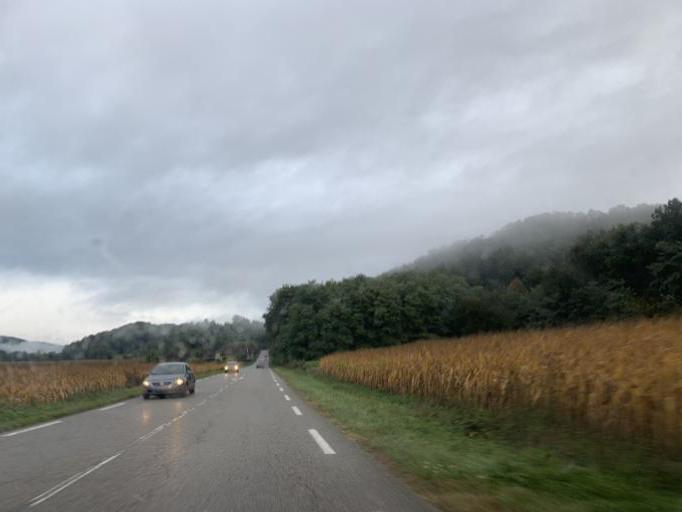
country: FR
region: Rhone-Alpes
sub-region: Departement de l'Ain
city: Belley
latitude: 45.7243
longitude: 5.6654
